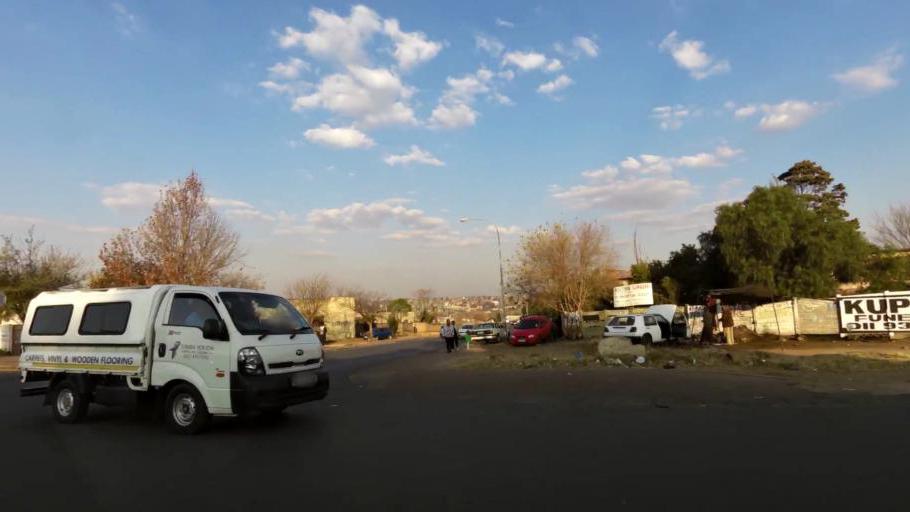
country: ZA
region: Gauteng
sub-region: City of Johannesburg Metropolitan Municipality
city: Soweto
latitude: -26.2251
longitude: 27.9088
